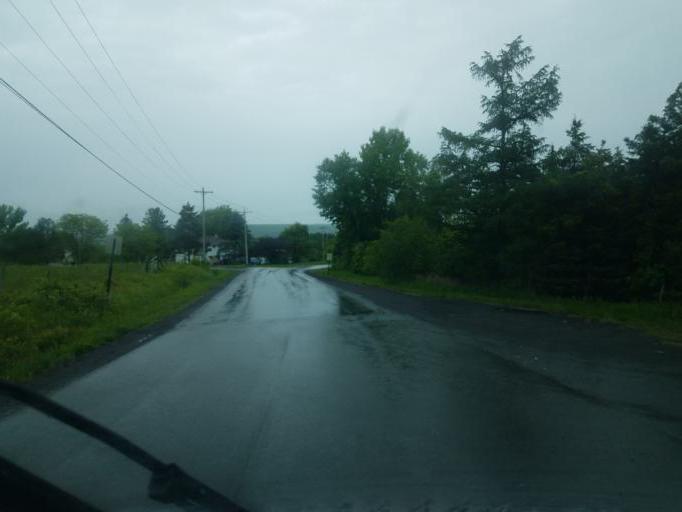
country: US
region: New York
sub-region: Herkimer County
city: Ilion
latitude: 42.9936
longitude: -75.0232
